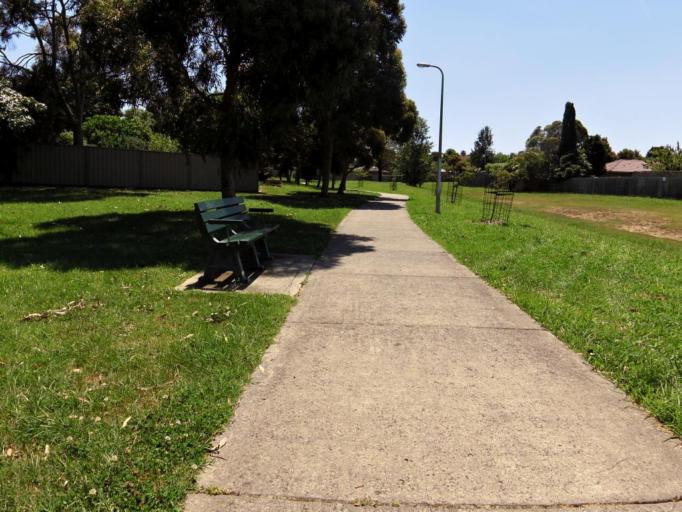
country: AU
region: Victoria
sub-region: Casey
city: Endeavour Hills
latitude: -37.9829
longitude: 145.2628
